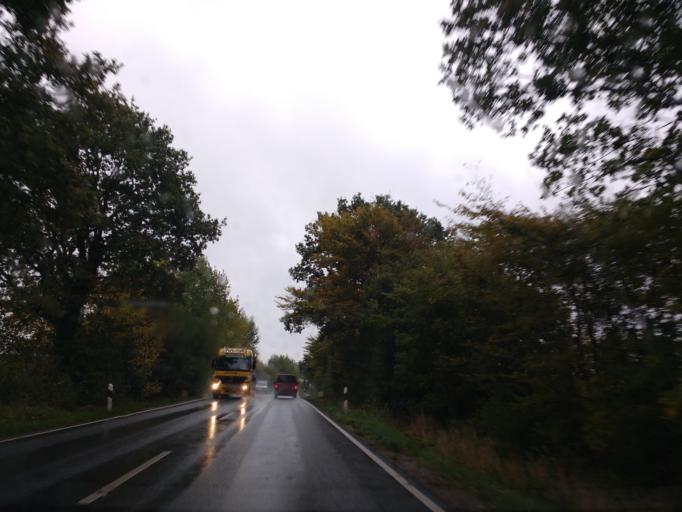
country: DE
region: Schleswig-Holstein
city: Eutin
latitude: 54.1110
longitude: 10.6598
